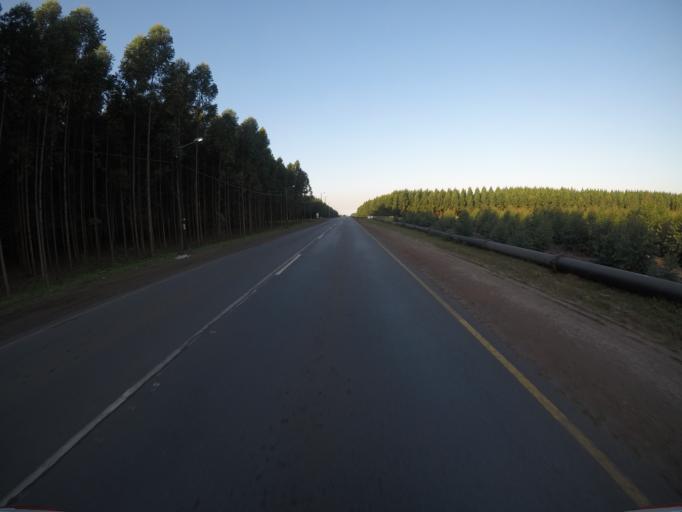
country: ZA
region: KwaZulu-Natal
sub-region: uThungulu District Municipality
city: KwaMbonambi
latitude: -28.6833
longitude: 32.1556
